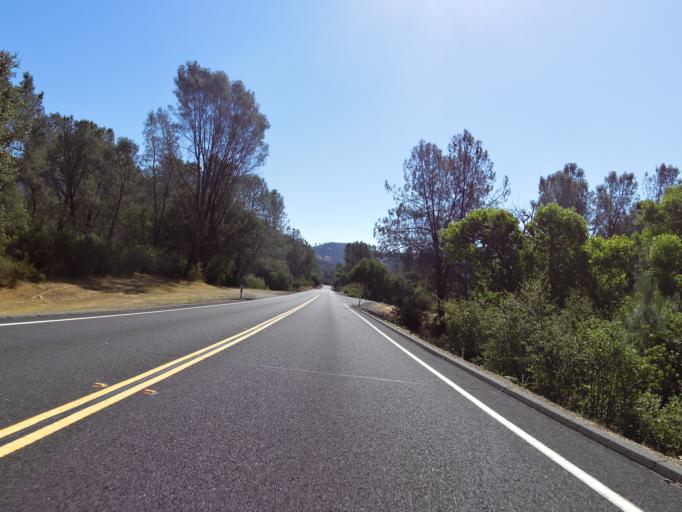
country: US
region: California
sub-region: Tuolumne County
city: Tuolumne City
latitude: 37.7012
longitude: -120.2581
